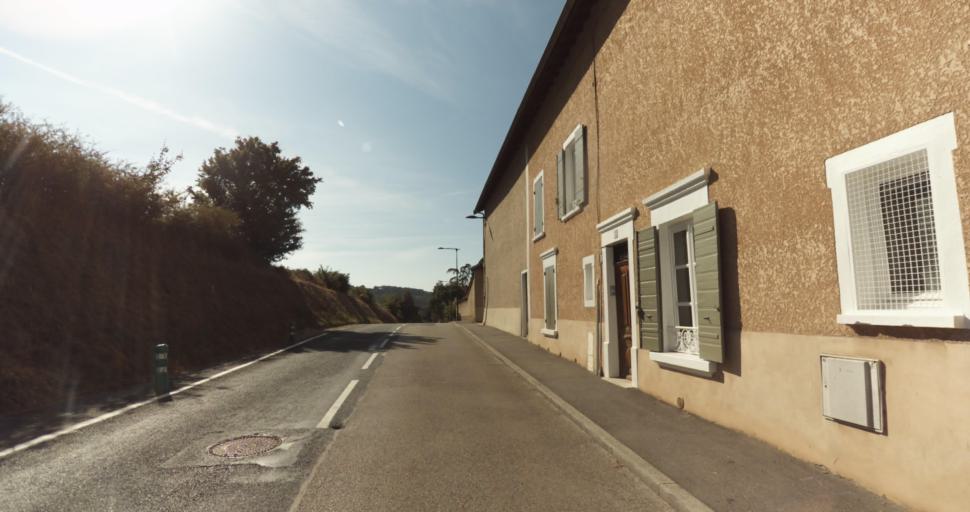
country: FR
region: Rhone-Alpes
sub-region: Departement du Rhone
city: Fleurieu-sur-Saone
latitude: 45.8695
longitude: 4.8425
